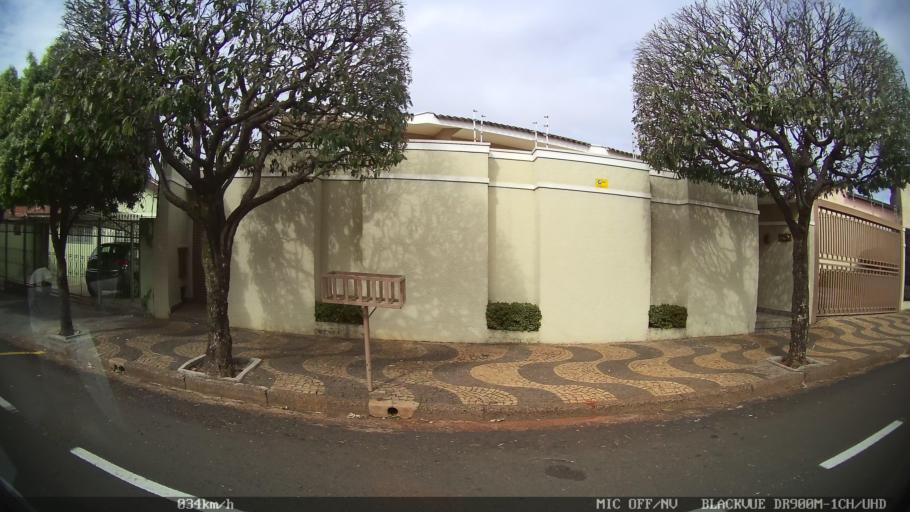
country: BR
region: Sao Paulo
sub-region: Sao Jose Do Rio Preto
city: Sao Jose do Rio Preto
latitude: -20.8167
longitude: -49.3688
